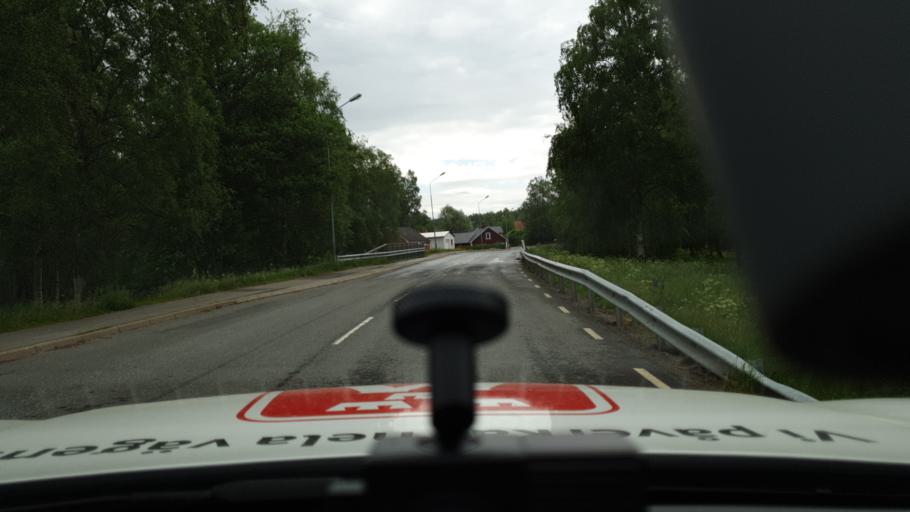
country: SE
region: Joenkoeping
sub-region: Mullsjo Kommun
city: Mullsjoe
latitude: 57.9889
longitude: 13.7665
